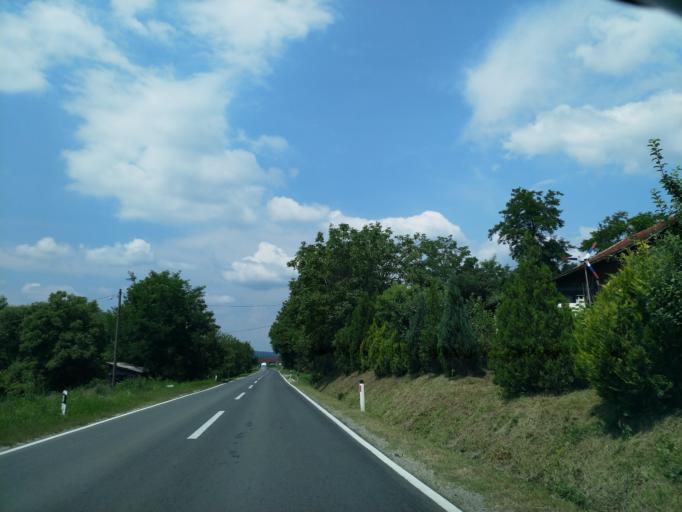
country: RS
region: Central Serbia
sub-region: Toplicki Okrug
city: Blace
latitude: 43.3543
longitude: 21.1776
